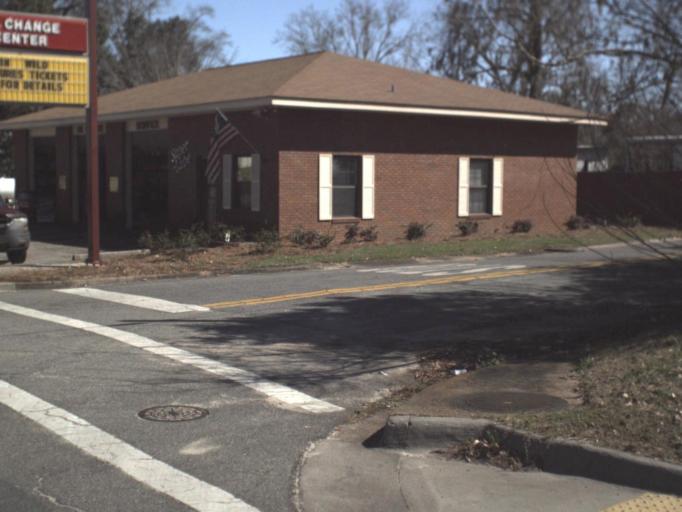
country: US
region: Florida
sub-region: Gadsden County
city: Quincy
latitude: 30.5880
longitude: -84.5858
